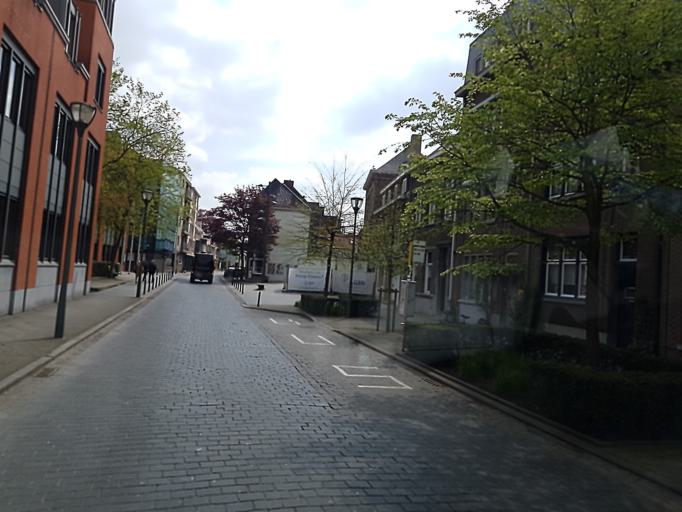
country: BE
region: Flanders
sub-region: Provincie Antwerpen
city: Turnhout
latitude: 51.3269
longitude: 4.9468
